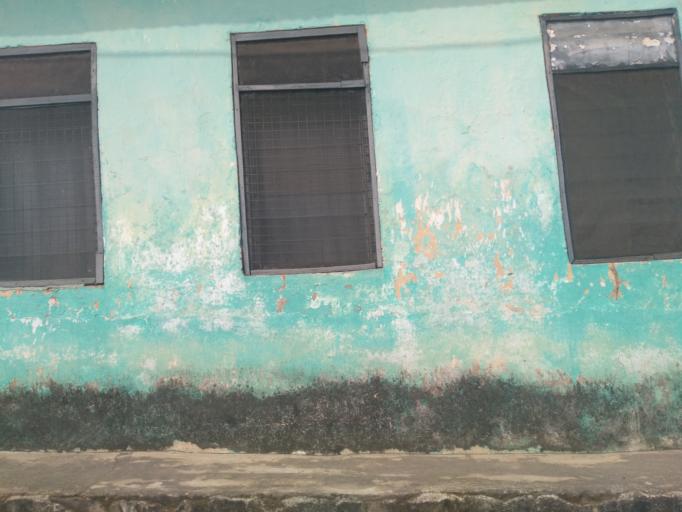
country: GH
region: Ashanti
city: Kumasi
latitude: 6.6850
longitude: -1.6025
